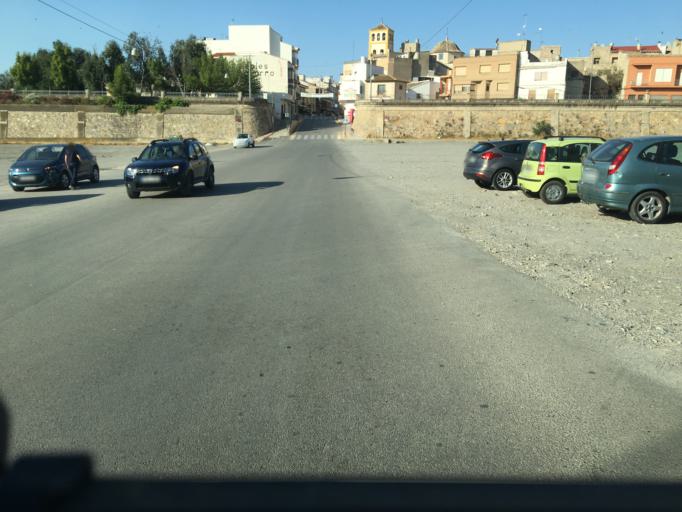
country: ES
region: Murcia
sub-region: Murcia
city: Puerto Lumbreras
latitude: 37.5611
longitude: -1.8097
